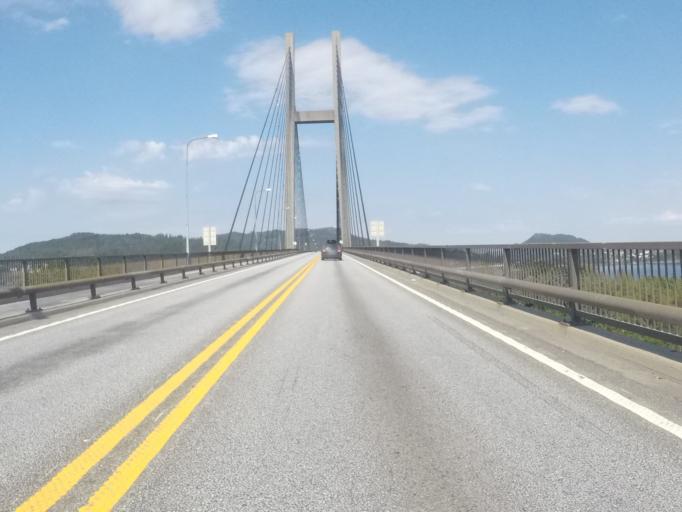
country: NO
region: Hordaland
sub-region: Lindas
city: Knarvik
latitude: 60.5193
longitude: 5.2756
